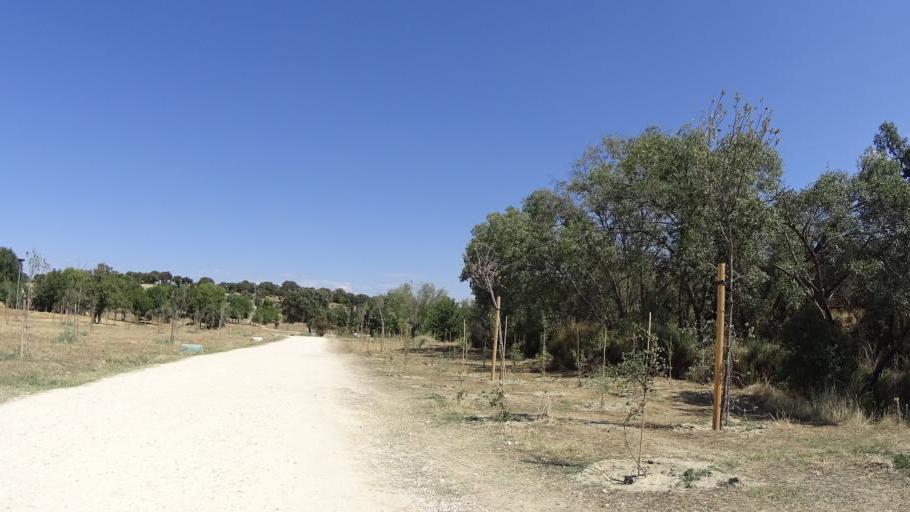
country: ES
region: Madrid
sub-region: Provincia de Madrid
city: Boadilla del Monte
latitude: 40.4074
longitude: -3.8708
